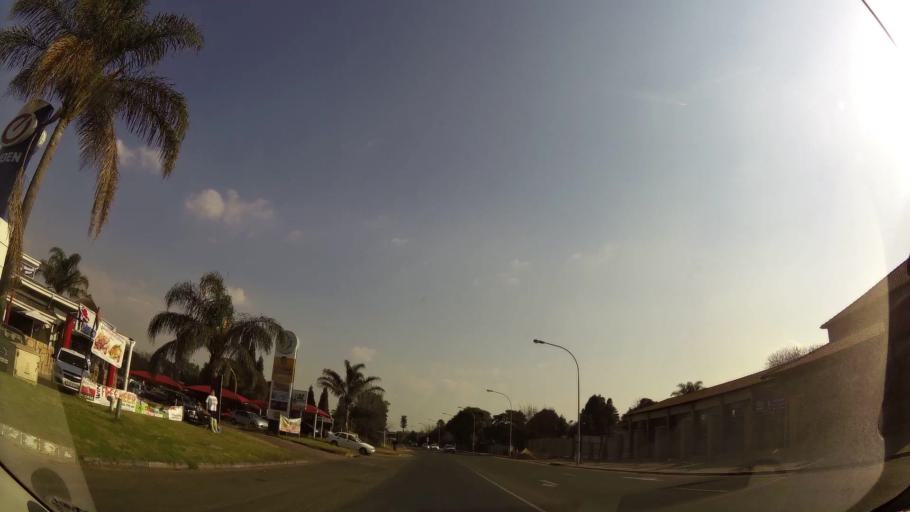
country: ZA
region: Gauteng
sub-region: Ekurhuleni Metropolitan Municipality
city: Benoni
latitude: -26.1498
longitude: 28.2990
